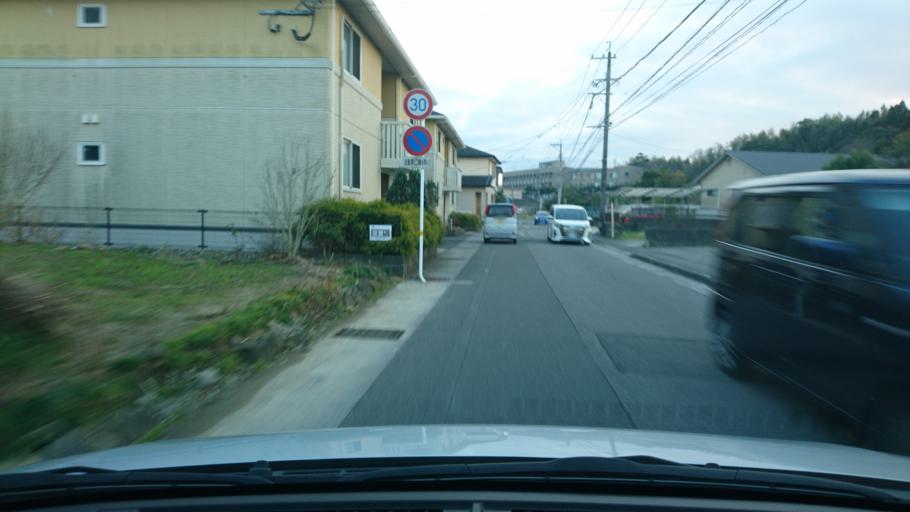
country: JP
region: Miyazaki
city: Miyazaki-shi
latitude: 31.8671
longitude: 131.4274
